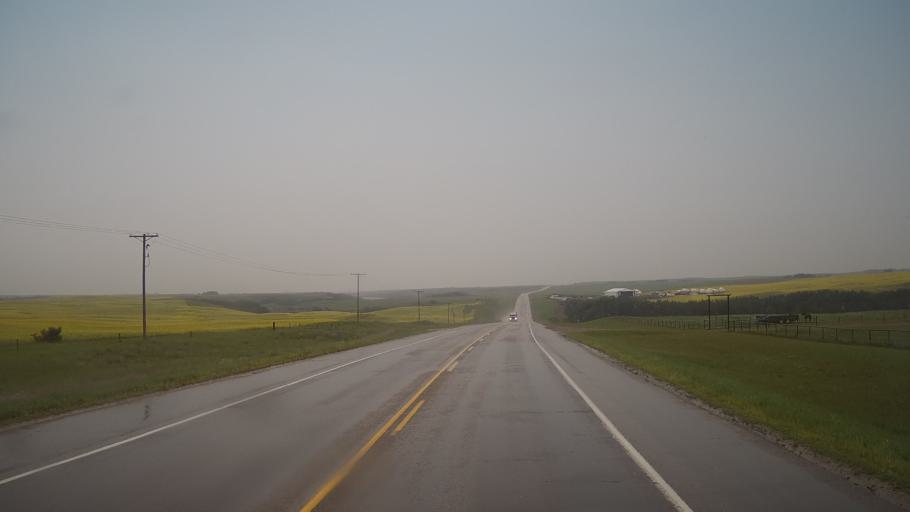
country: CA
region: Saskatchewan
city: Biggar
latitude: 52.0680
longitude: -108.0047
